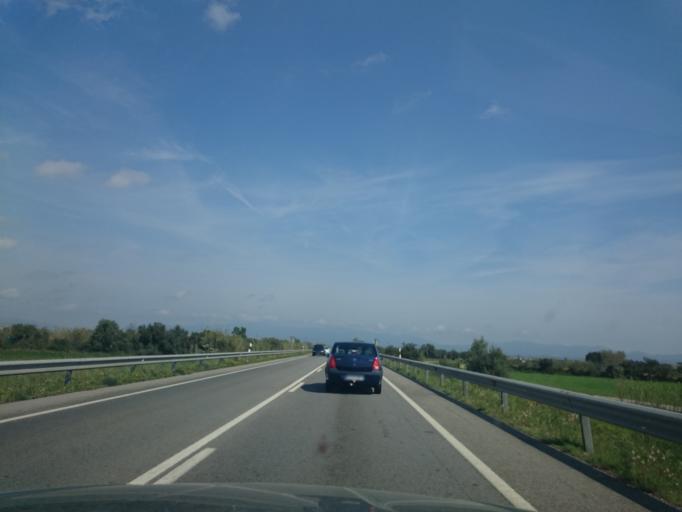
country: ES
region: Catalonia
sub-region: Provincia de Girona
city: Vilamalla
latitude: 42.2434
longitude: 2.9841
